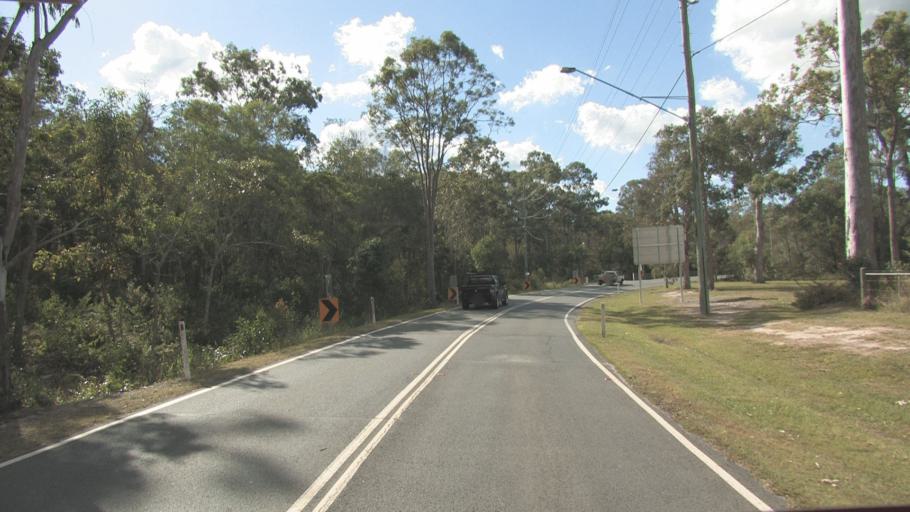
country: AU
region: Queensland
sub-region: Logan
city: Beenleigh
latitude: -27.6571
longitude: 153.2214
